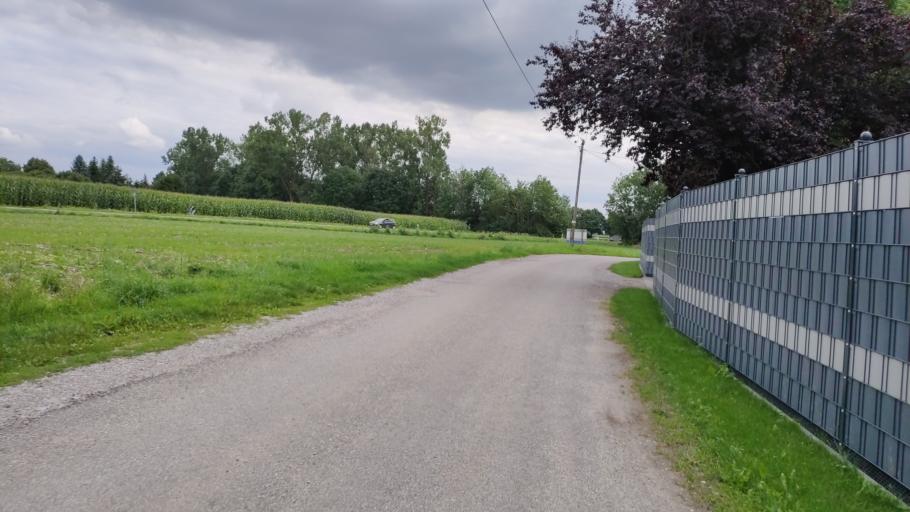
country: DE
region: Bavaria
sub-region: Swabia
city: Konigsbrunn
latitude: 48.2607
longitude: 10.9044
